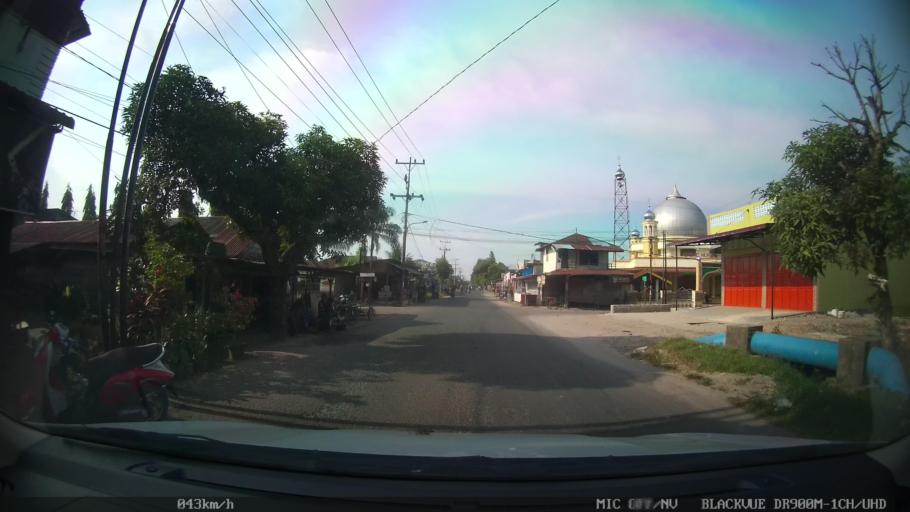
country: ID
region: North Sumatra
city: Binjai
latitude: 3.6157
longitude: 98.5183
